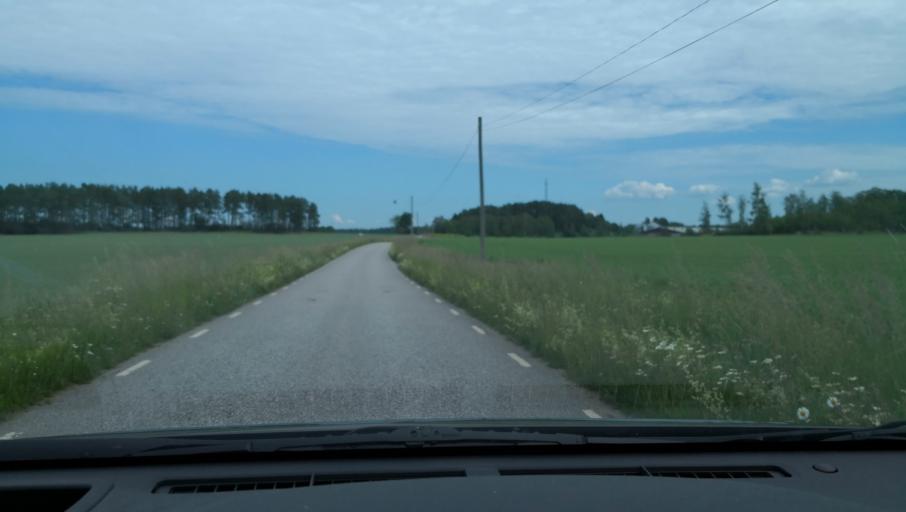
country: SE
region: Uppsala
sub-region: Enkopings Kommun
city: Orsundsbro
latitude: 59.6936
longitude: 17.3940
